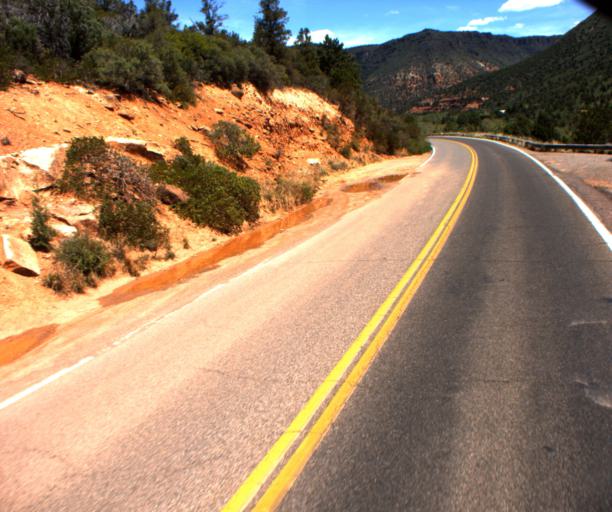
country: US
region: Arizona
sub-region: Coconino County
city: Sedona
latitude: 34.8935
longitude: -111.7331
